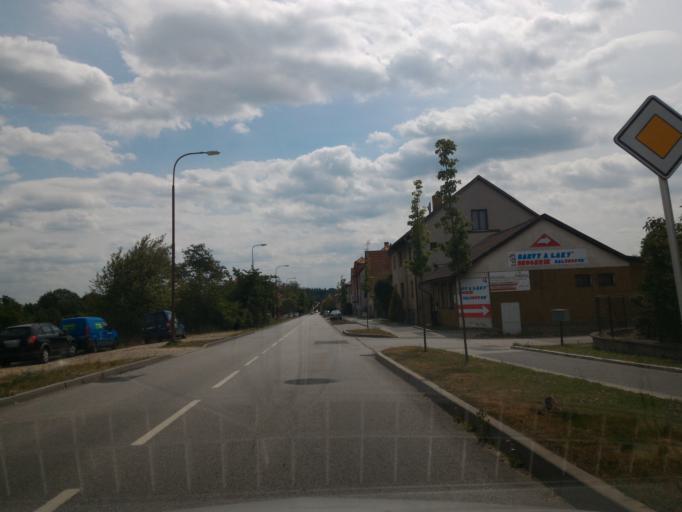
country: CZ
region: Vysocina
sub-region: Okres Jihlava
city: Telc
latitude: 49.1833
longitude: 15.4434
